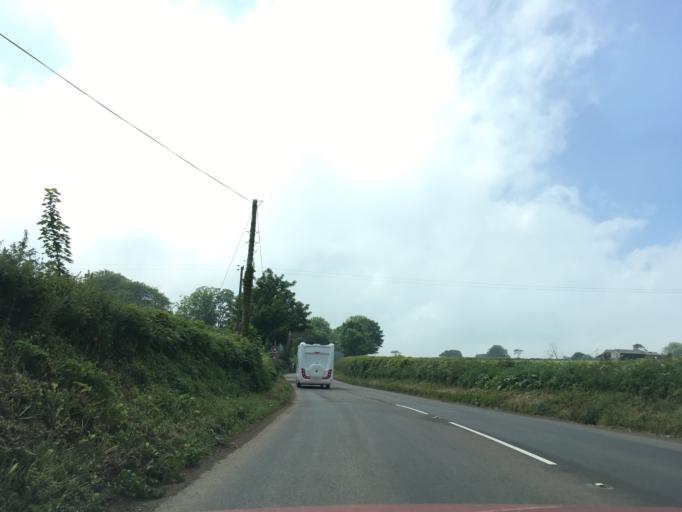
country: GB
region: England
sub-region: Devon
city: Totnes
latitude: 50.4224
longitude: -3.6987
